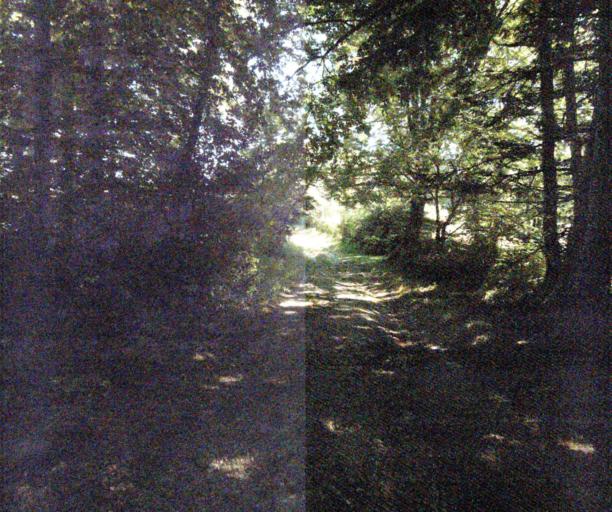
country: FR
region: Midi-Pyrenees
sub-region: Departement du Tarn
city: Dourgne
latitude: 43.4370
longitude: 2.1286
